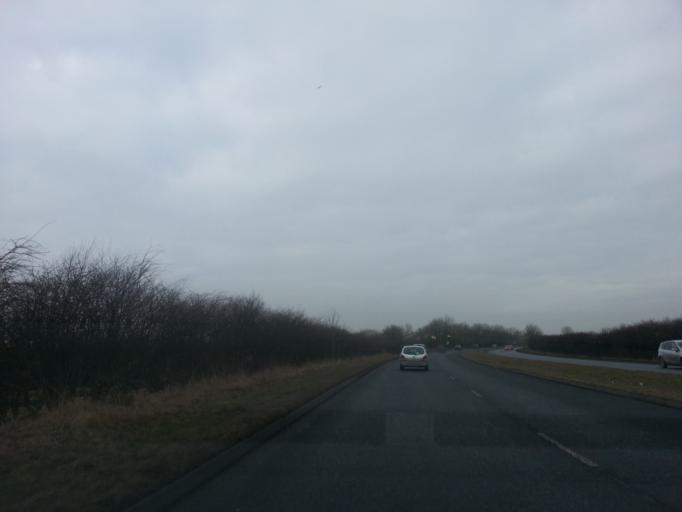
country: GB
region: England
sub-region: Darlington
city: Heighington
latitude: 54.5677
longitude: -1.6058
